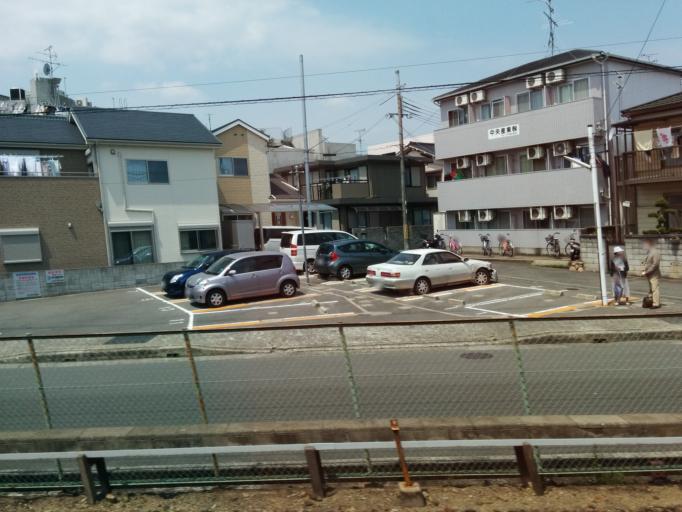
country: JP
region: Osaka
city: Ibaraki
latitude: 34.8288
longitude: 135.5862
